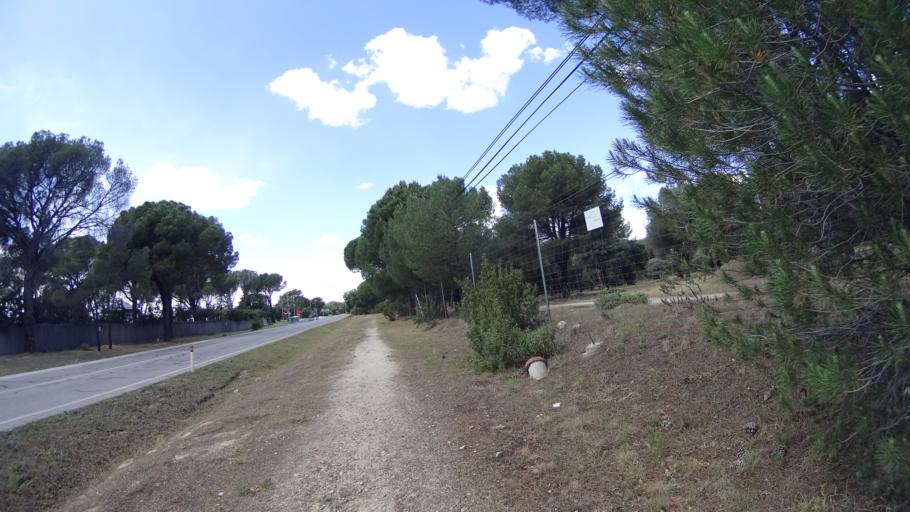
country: ES
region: Madrid
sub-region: Provincia de Madrid
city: Boadilla del Monte
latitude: 40.4327
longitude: -3.8719
